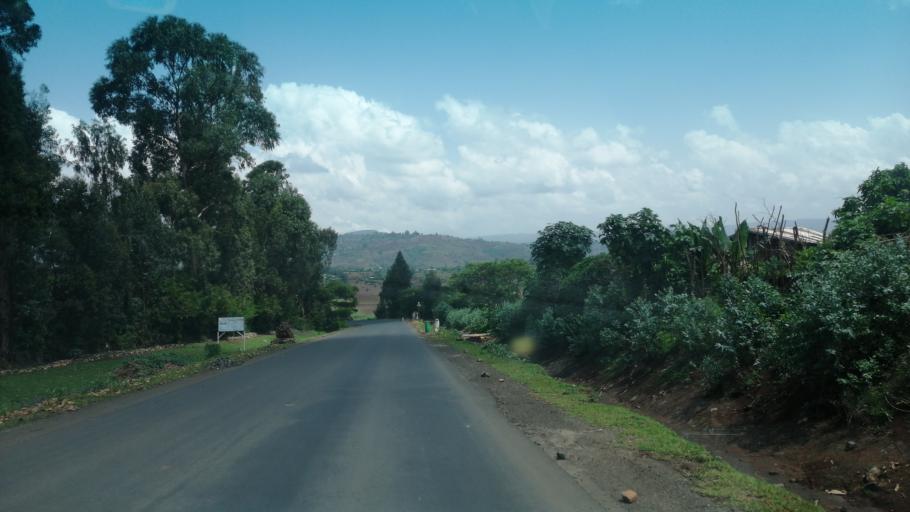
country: ET
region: Oromiya
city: Gedo
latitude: 8.9765
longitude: 37.5618
